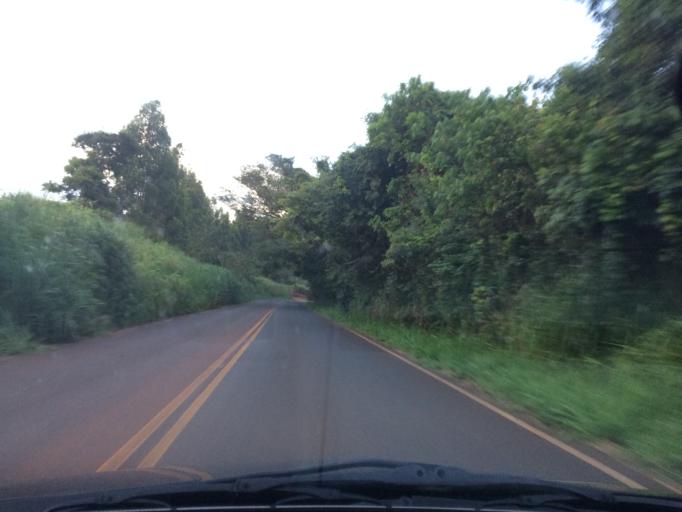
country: BR
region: Sao Paulo
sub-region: Tambau
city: Tambau
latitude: -21.7255
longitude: -47.1861
